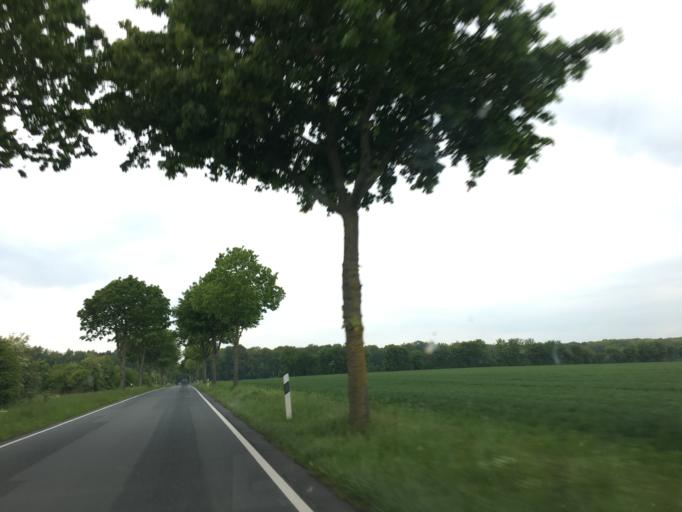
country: DE
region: Lower Saxony
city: Haste
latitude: 52.3801
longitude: 9.4266
